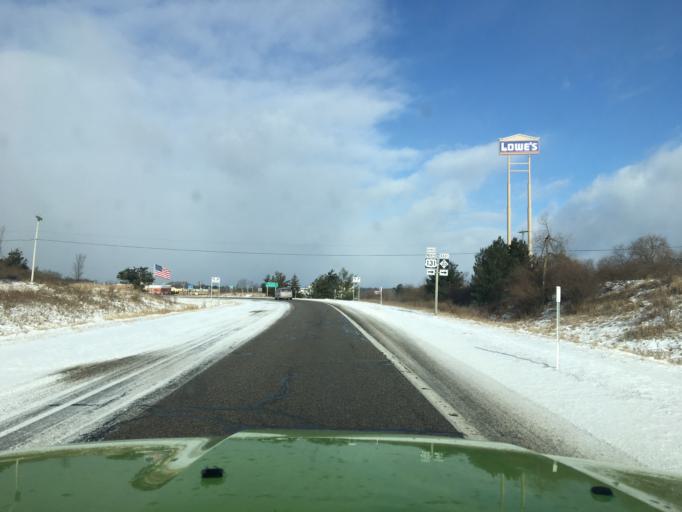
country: US
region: Michigan
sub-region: Mecosta County
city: Big Rapids
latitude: 43.6851
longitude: -85.5180
